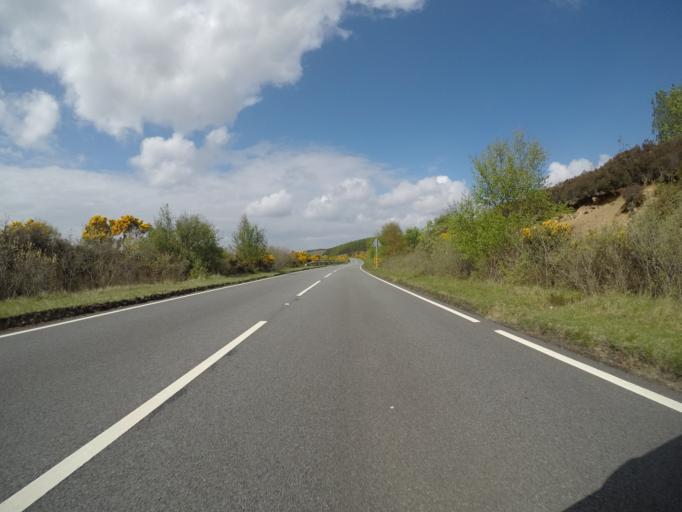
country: GB
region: Scotland
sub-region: Highland
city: Portree
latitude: 57.5213
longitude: -6.3415
